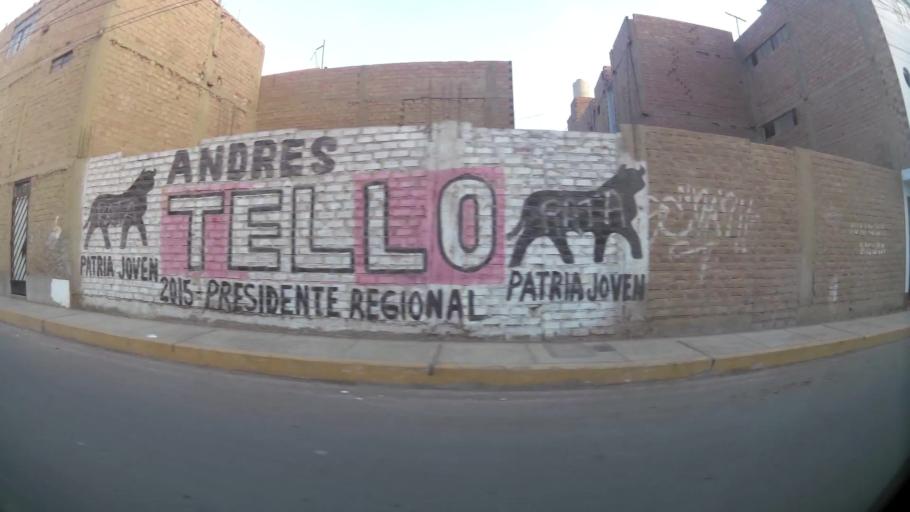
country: PE
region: Lima
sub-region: Huaura
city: Huacho
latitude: -11.1175
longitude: -77.6078
